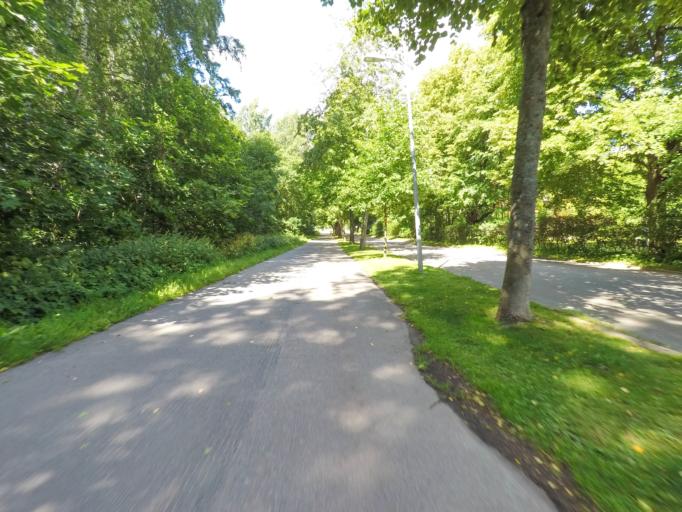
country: FI
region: Uusimaa
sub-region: Helsinki
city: Vantaa
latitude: 60.2173
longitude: 25.0951
